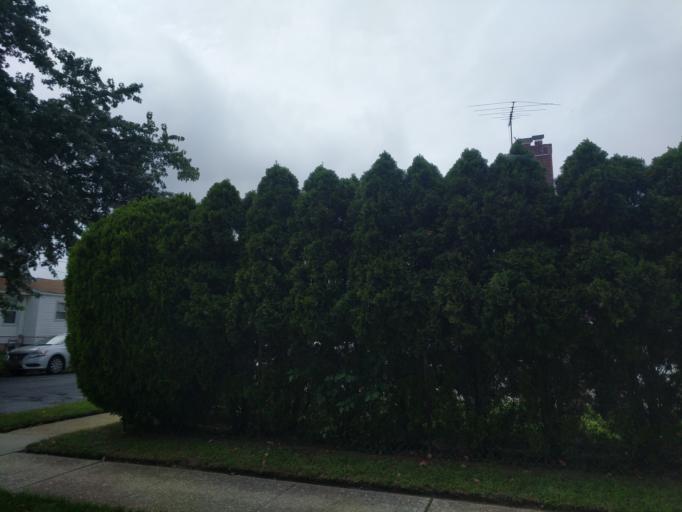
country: US
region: New York
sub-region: Nassau County
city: Valley Stream
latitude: 40.6659
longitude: -73.6956
